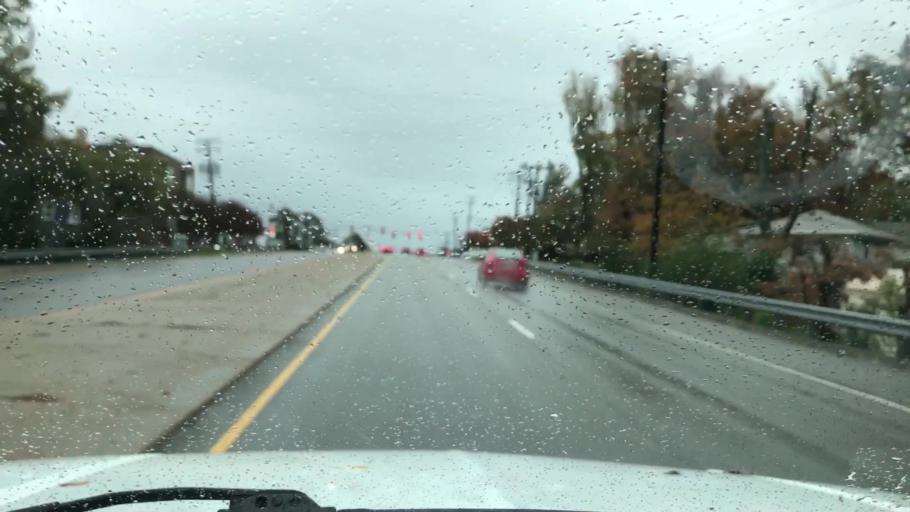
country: US
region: Virginia
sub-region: Henrico County
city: Tuckahoe
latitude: 37.5948
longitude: -77.5687
